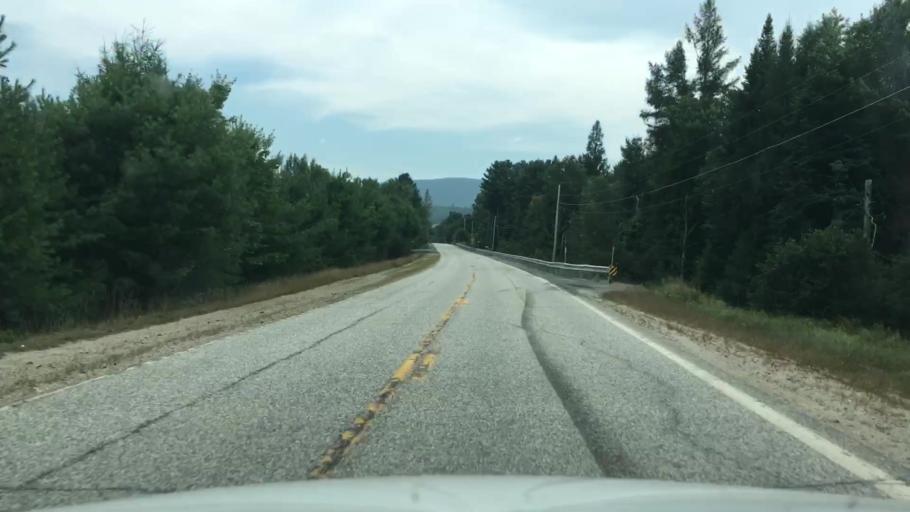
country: US
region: Maine
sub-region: Oxford County
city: Rumford
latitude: 44.5976
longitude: -70.7375
